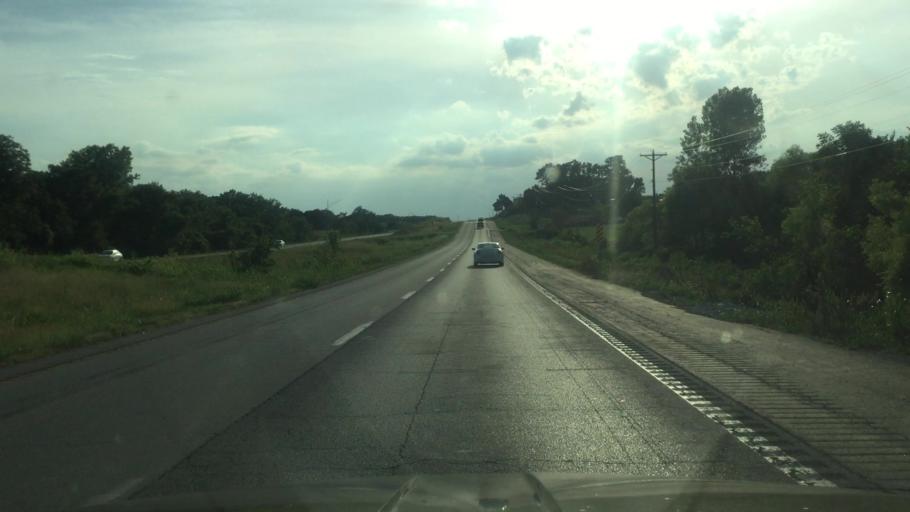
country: US
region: Missouri
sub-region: Jackson County
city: Lone Jack
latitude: 38.8702
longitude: -94.1252
